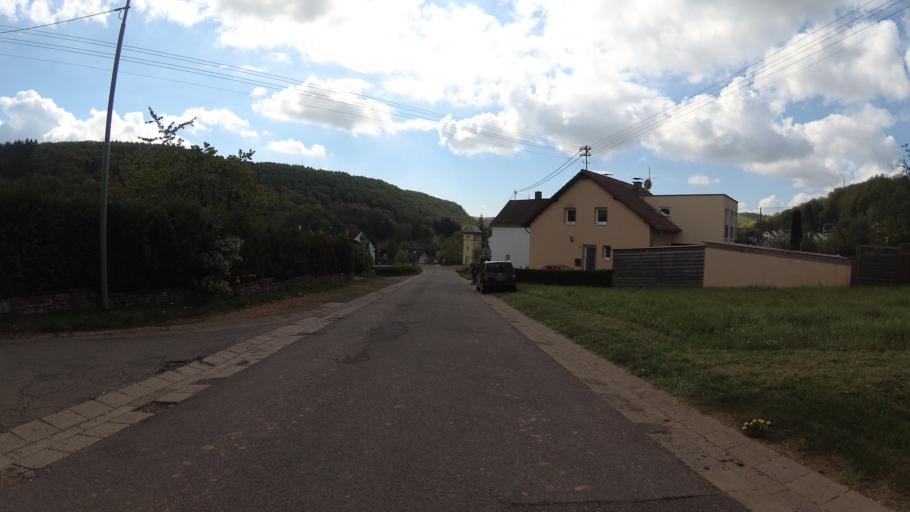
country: DE
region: Saarland
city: Wadern
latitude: 49.4961
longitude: 6.8646
